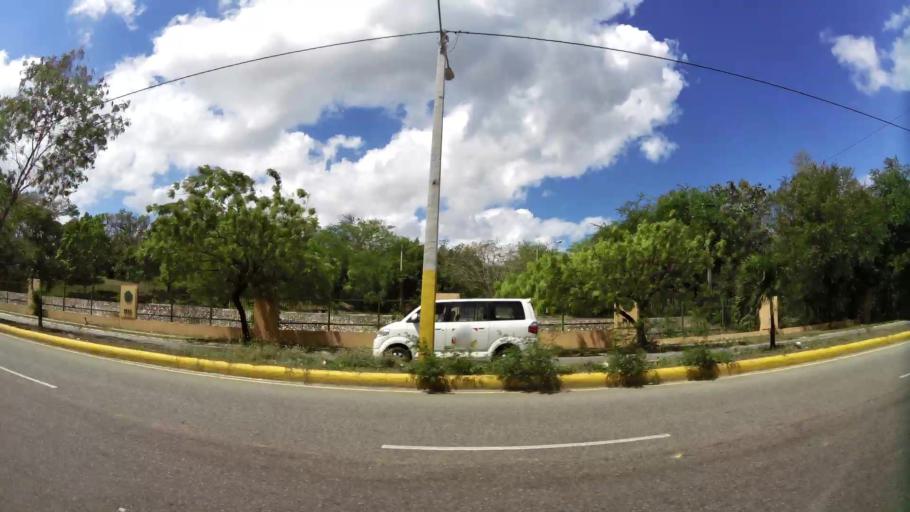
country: DO
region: Nacional
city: La Agustina
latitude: 18.5200
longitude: -69.9228
